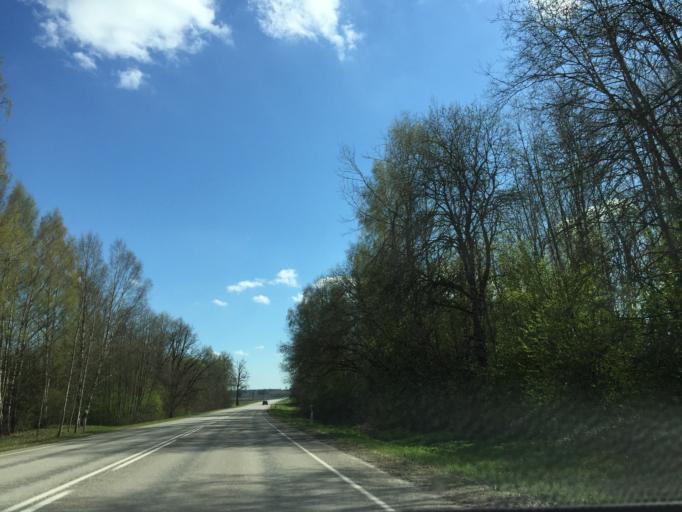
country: EE
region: Valgamaa
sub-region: Valga linn
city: Valga
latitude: 57.8858
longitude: 26.0584
